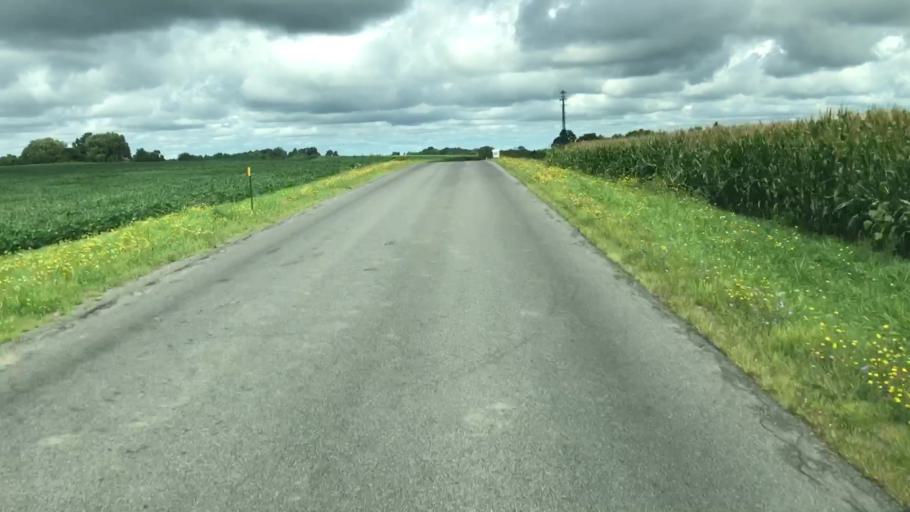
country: US
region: New York
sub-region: Onondaga County
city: Skaneateles
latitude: 42.9378
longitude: -76.4709
